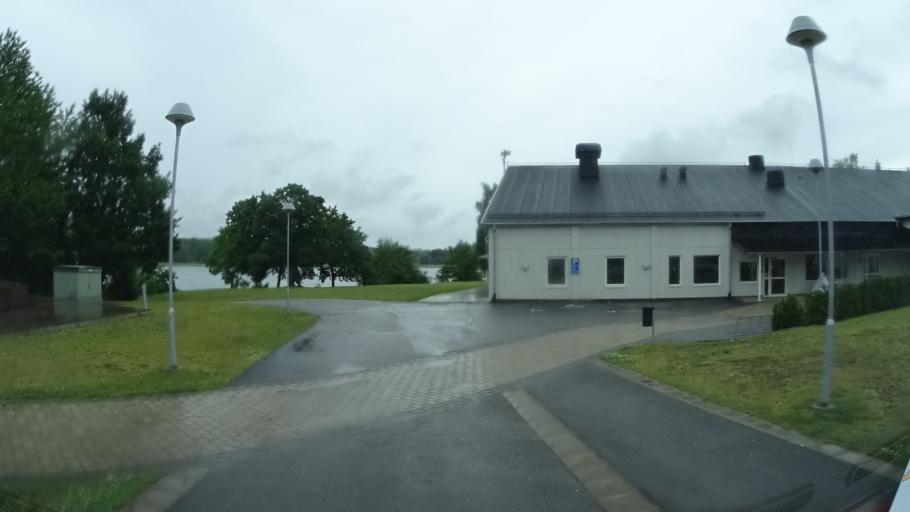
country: SE
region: Kalmar
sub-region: Vasterviks Kommun
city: Gamleby
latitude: 57.8901
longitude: 16.4181
